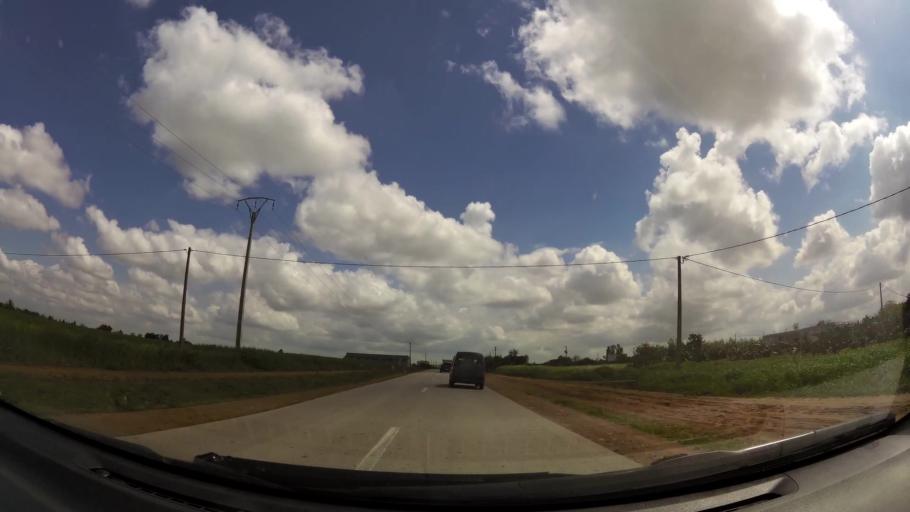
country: MA
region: Chaouia-Ouardigha
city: Nouaseur
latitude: 33.3342
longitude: -7.7373
